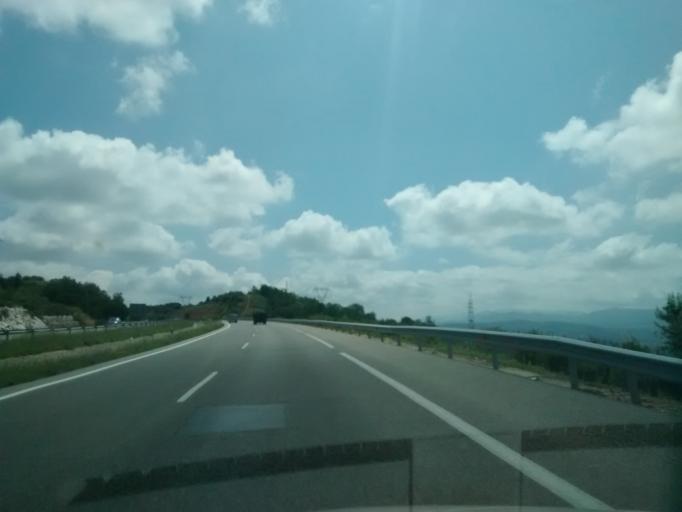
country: ES
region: Castille and Leon
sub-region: Provincia de Leon
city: Ponferrada
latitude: 42.5696
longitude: -6.5950
